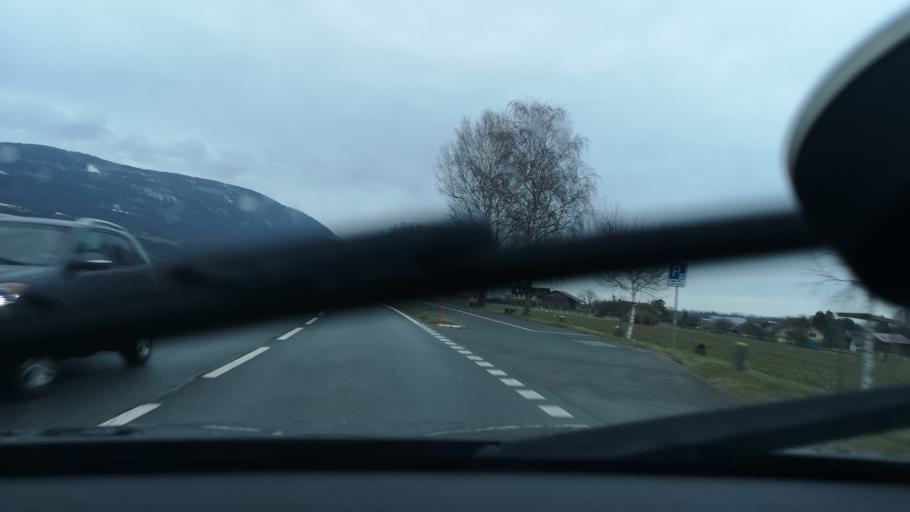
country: CH
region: Vaud
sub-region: Jura-Nord vaudois District
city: Grandson
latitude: 46.8183
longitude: 6.6573
